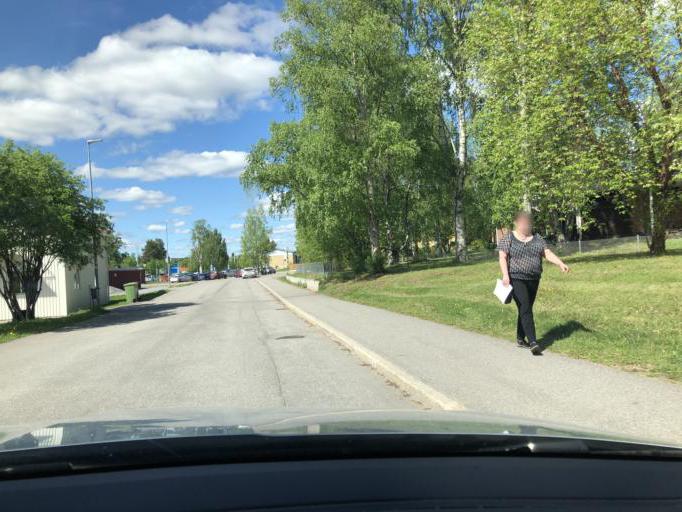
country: SE
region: Norrbotten
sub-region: Alvsbyns Kommun
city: AElvsbyn
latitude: 65.6695
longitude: 21.0115
